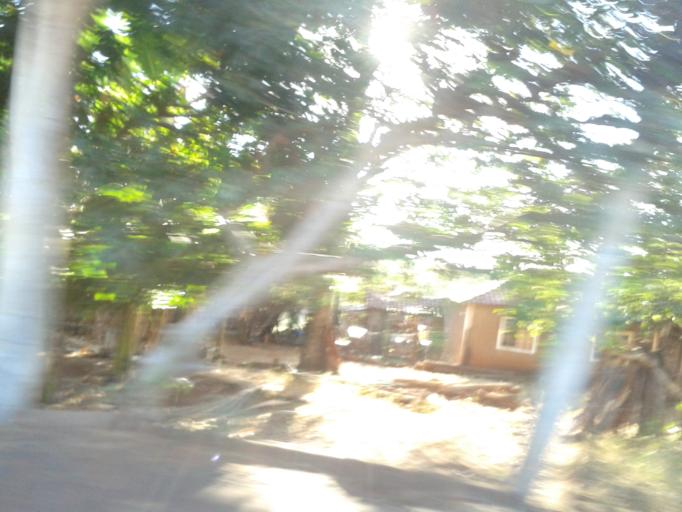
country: BR
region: Minas Gerais
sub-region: Centralina
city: Centralina
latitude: -18.7236
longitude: -49.2069
